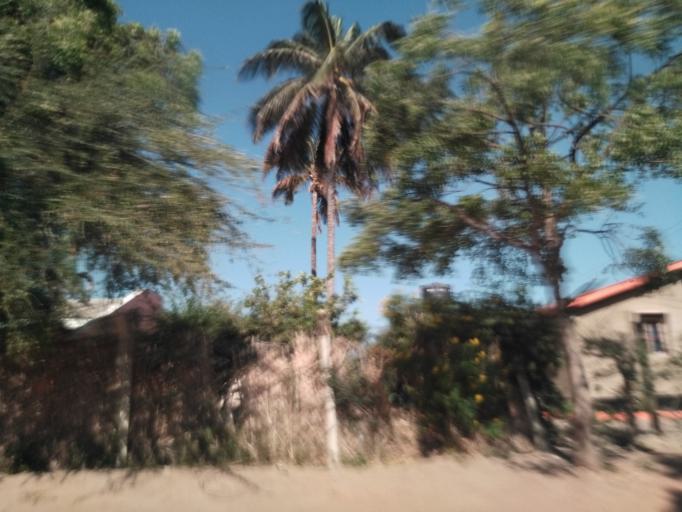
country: TZ
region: Dodoma
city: Dodoma
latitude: -6.1596
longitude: 35.7516
